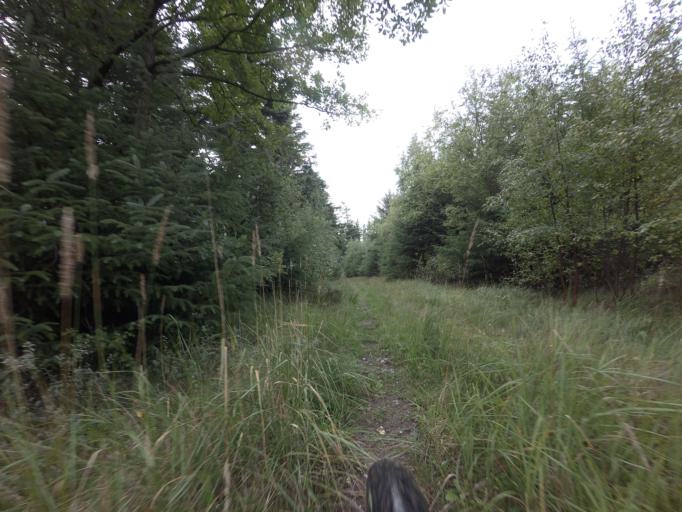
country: DK
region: North Denmark
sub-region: Hjorring Kommune
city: Hirtshals
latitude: 57.5779
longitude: 10.0425
